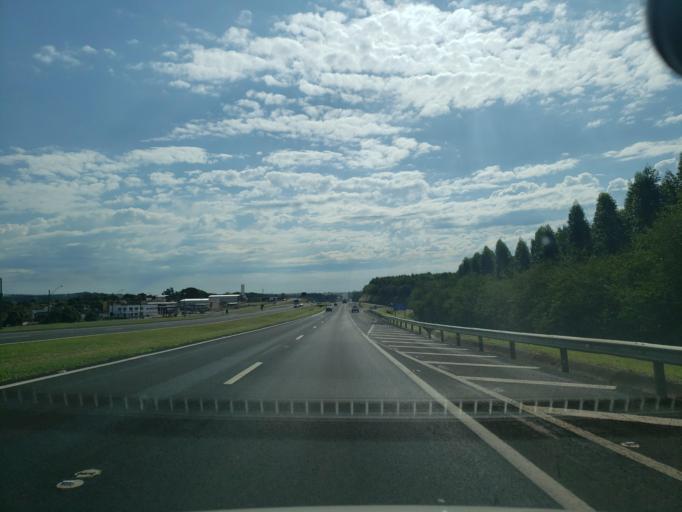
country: BR
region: Sao Paulo
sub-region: Pirajui
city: Pirajui
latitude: -21.9944
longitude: -49.4366
